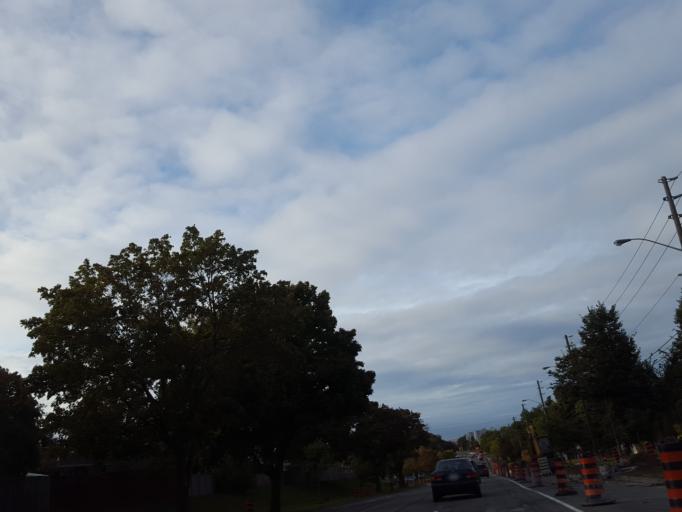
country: CA
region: Ontario
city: Scarborough
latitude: 43.7742
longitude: -79.3058
